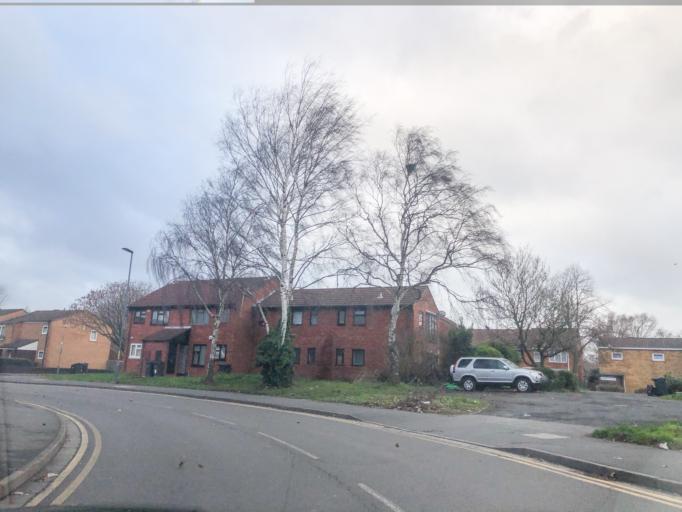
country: GB
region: England
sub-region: City and Borough of Birmingham
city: Birmingham
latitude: 52.4600
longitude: -1.8931
